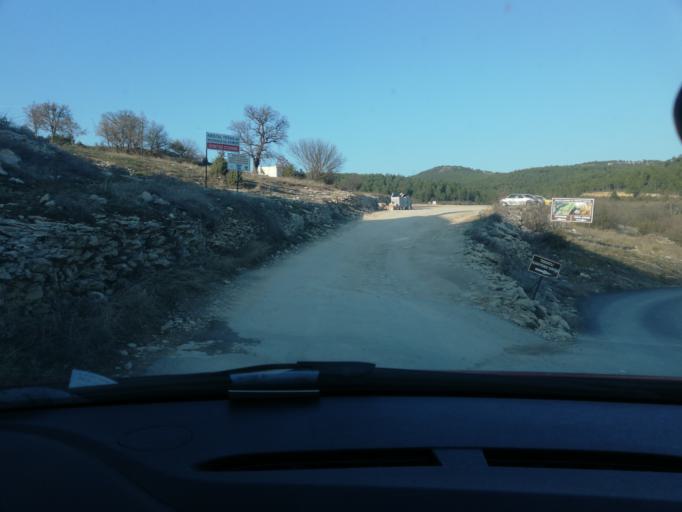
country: TR
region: Karabuk
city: Safranbolu
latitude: 41.2802
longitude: 32.6828
